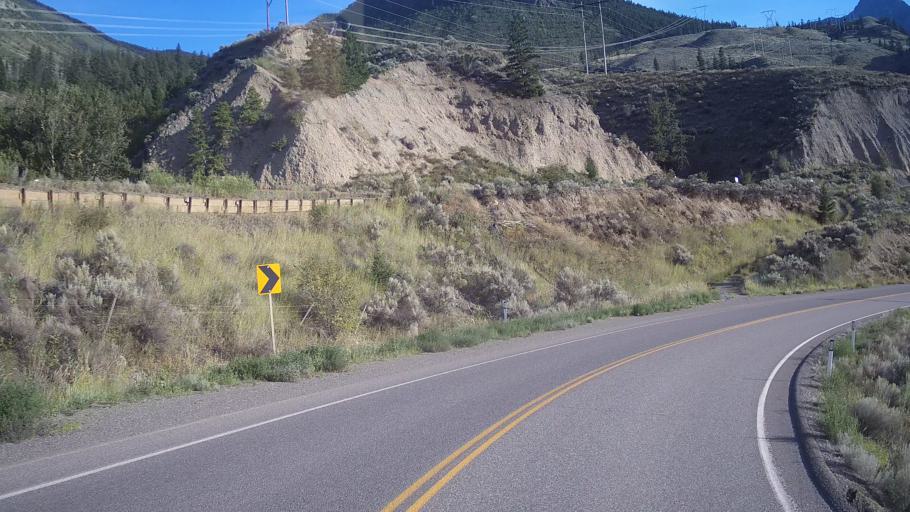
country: CA
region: British Columbia
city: Lillooet
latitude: 50.7562
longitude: -121.8328
